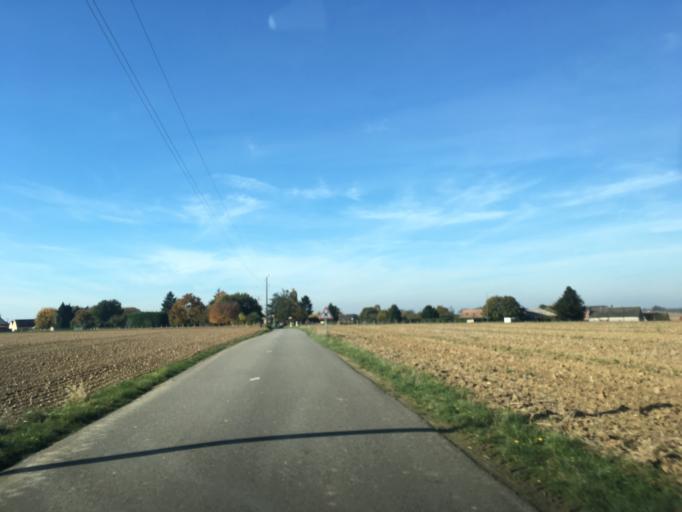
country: FR
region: Haute-Normandie
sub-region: Departement de l'Eure
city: Heudreville-sur-Eure
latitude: 49.1593
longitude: 1.2536
